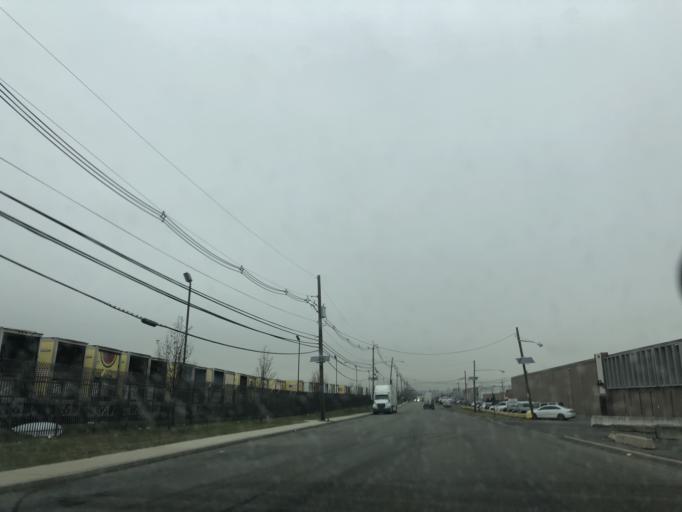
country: US
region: New Jersey
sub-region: Union County
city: Elizabeth
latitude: 40.6633
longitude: -74.1861
